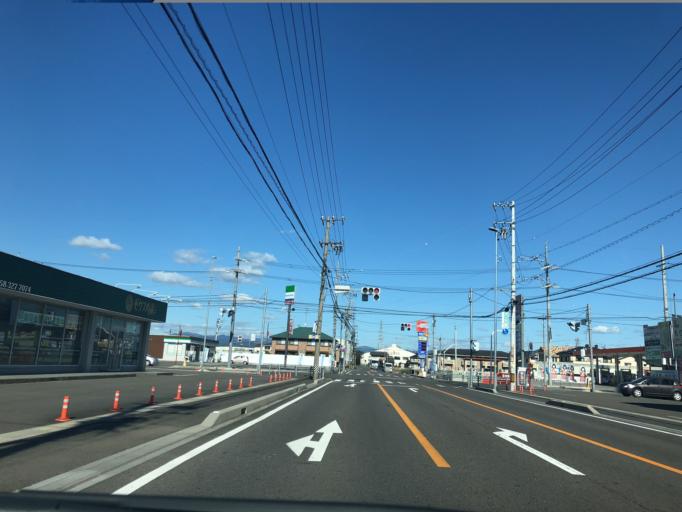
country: JP
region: Gifu
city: Ogaki
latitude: 35.3943
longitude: 136.6660
